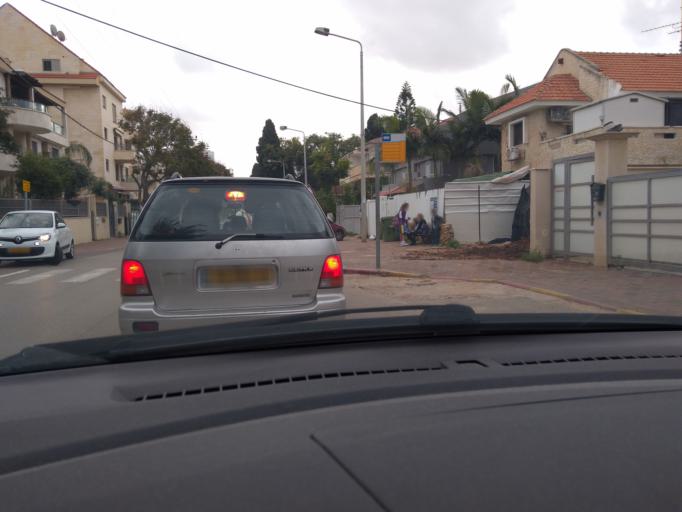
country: IL
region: Central District
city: Netanya
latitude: 32.3447
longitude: 34.8624
